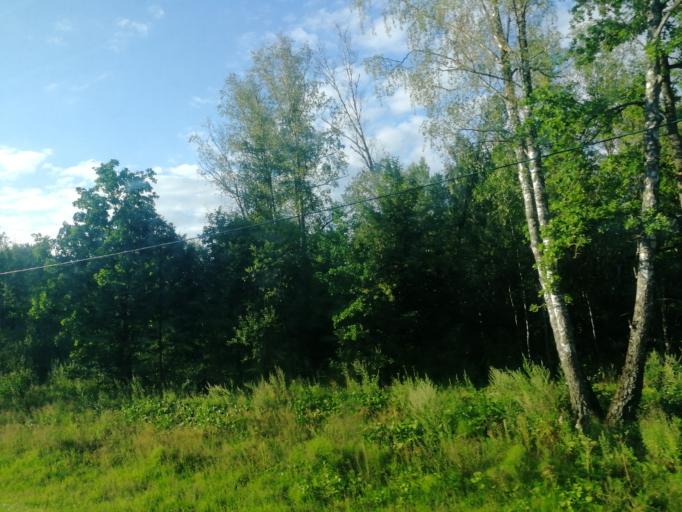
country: RU
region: Kaluga
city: Kaluga
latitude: 54.4411
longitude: 36.3291
